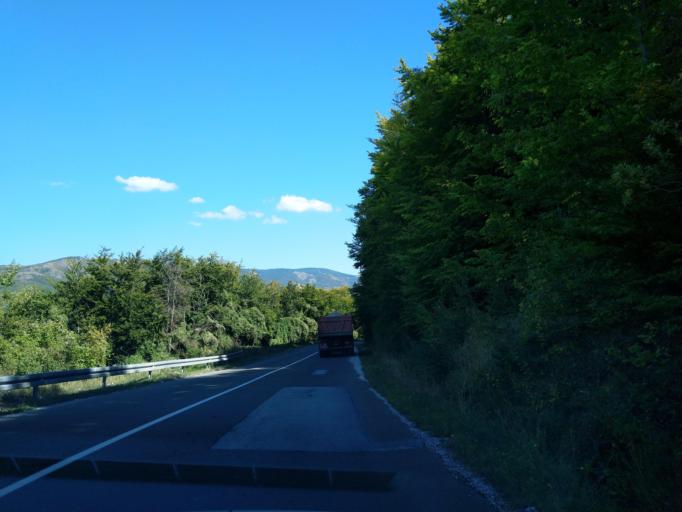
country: RS
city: Sokolovica
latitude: 43.2510
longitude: 20.2433
